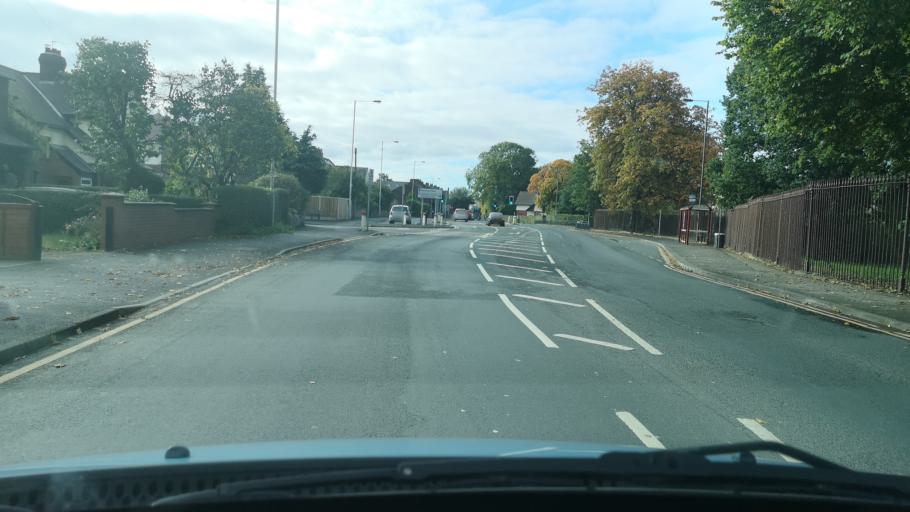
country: GB
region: England
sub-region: City and Borough of Wakefield
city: Wakefield
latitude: 53.6921
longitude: -1.4855
